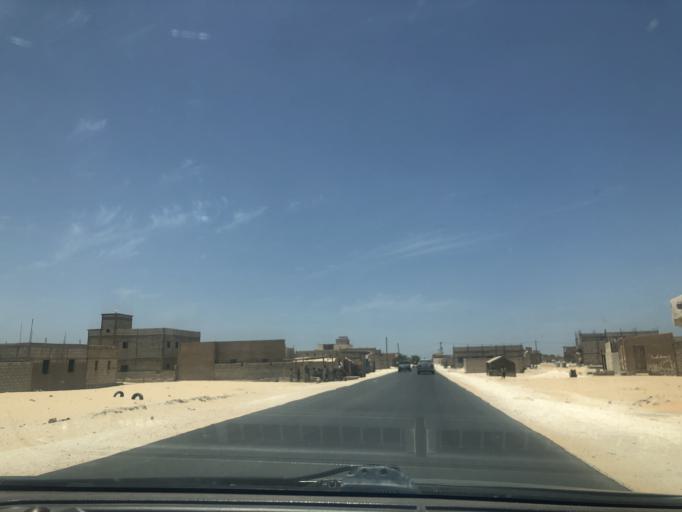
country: MR
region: Nouakchott
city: Nouakchott
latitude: 18.0034
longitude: -15.9625
